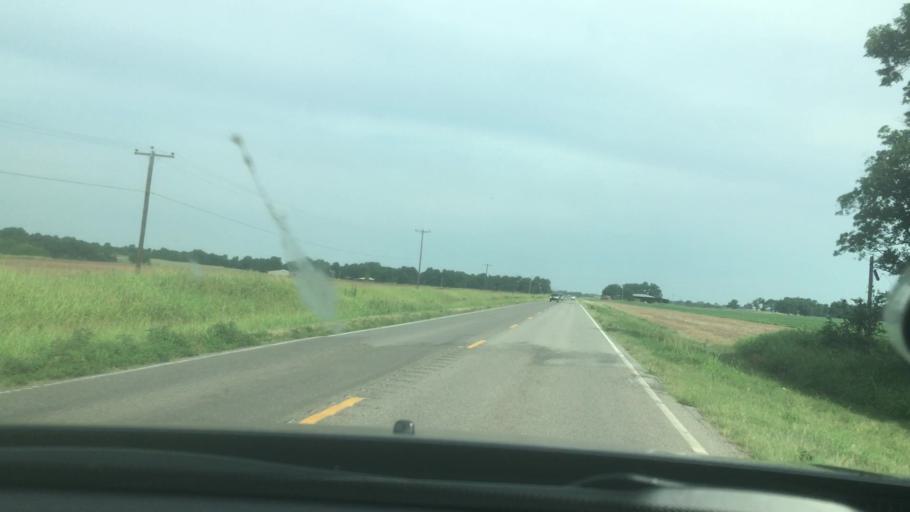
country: US
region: Oklahoma
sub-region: Garvin County
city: Maysville
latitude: 34.7853
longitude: -97.3356
